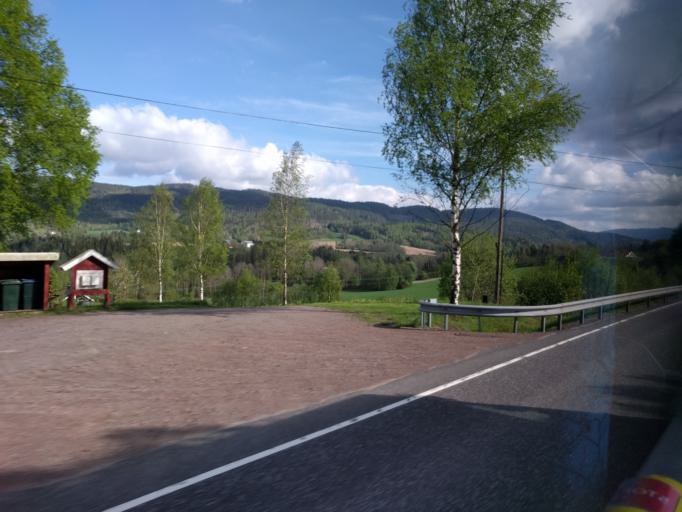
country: NO
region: Vestfold
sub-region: Lardal
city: Svarstad
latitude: 59.3529
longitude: 9.9110
